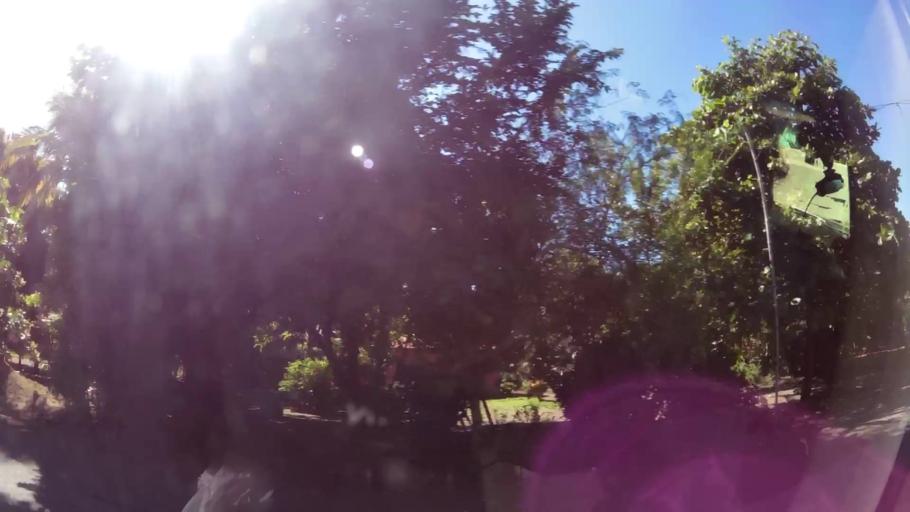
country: GT
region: Santa Rosa
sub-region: Municipio de Taxisco
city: Taxisco
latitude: 13.9112
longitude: -90.5300
